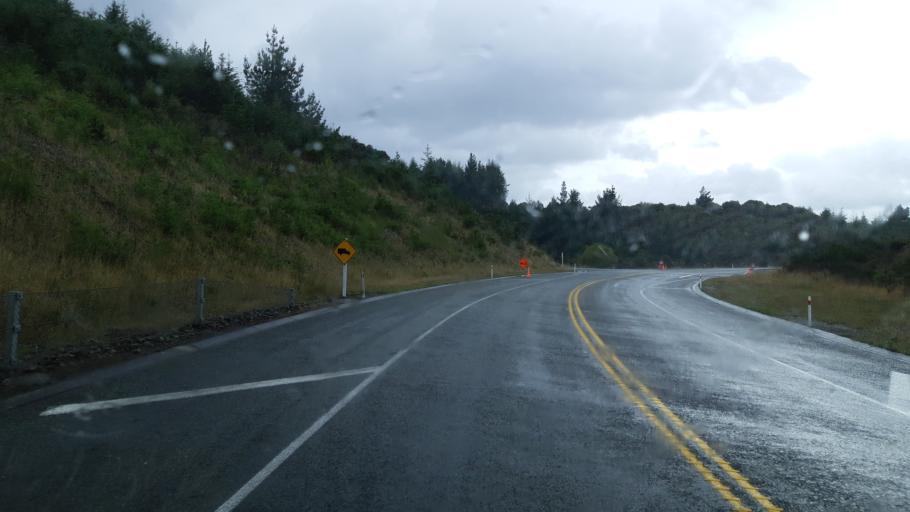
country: NZ
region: Tasman
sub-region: Tasman District
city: Wakefield
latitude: -41.4804
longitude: 172.9072
